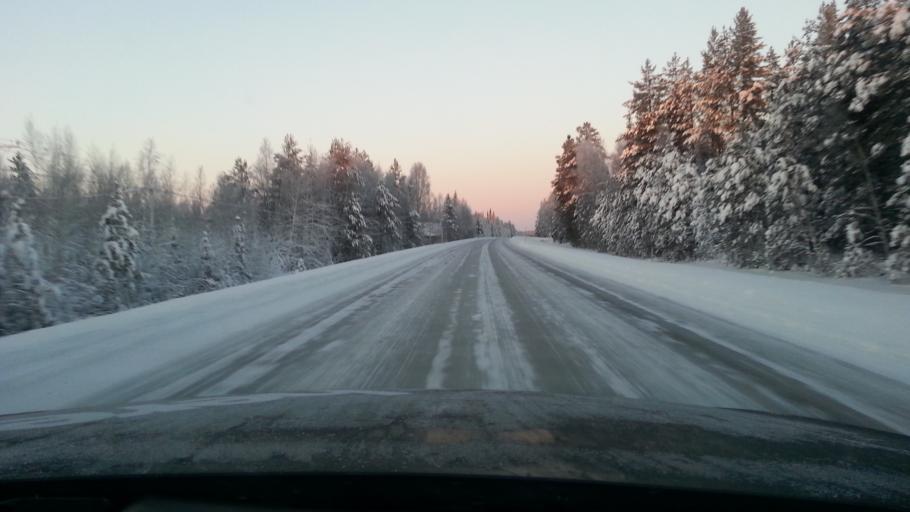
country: FI
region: Lapland
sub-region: Tunturi-Lappi
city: Kittilae
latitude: 67.2178
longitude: 24.9243
